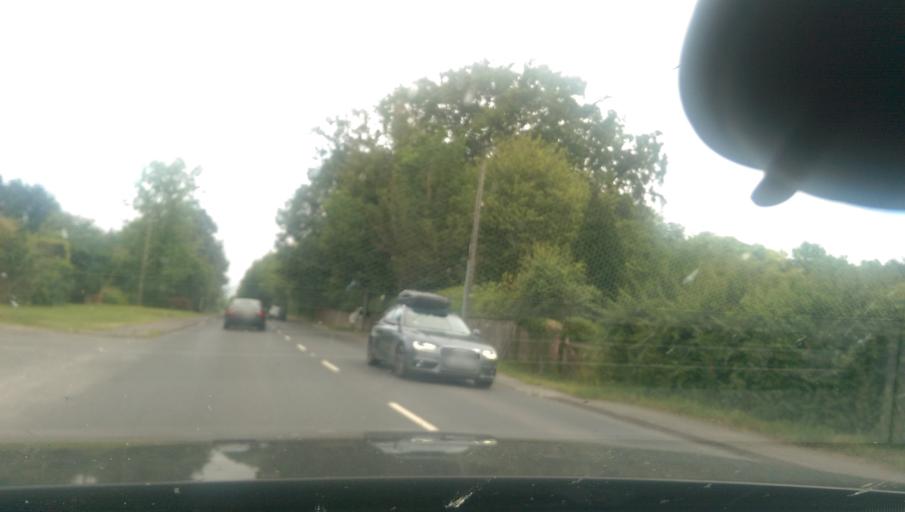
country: GB
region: England
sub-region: Wiltshire
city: Amesbury
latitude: 51.1861
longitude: -1.7833
